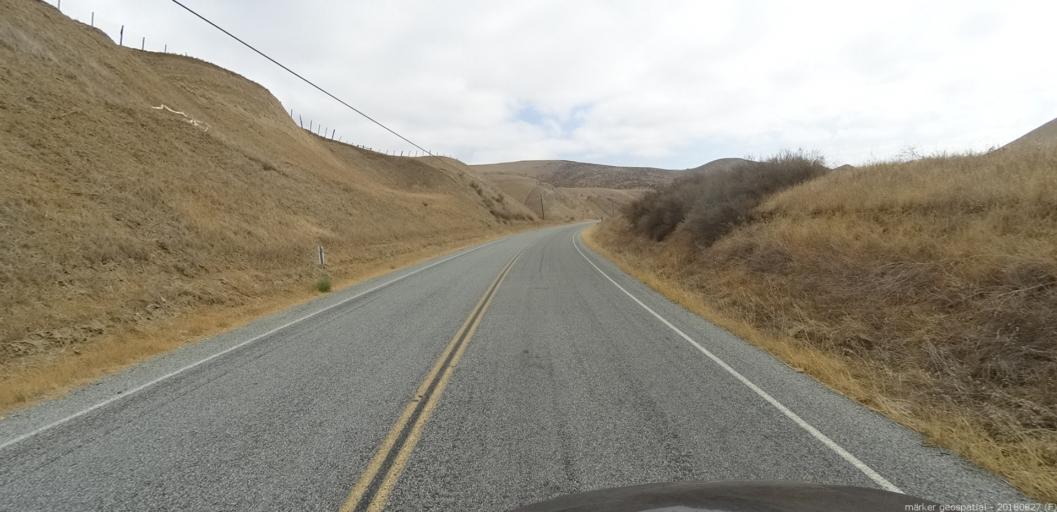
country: US
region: California
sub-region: Monterey County
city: King City
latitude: 36.2663
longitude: -121.0785
